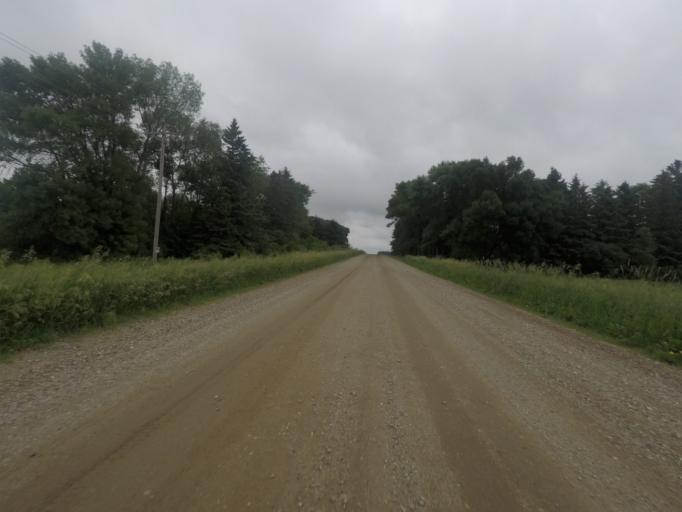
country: US
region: Minnesota
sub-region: Steele County
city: Owatonna
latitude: 44.0373
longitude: -93.0899
